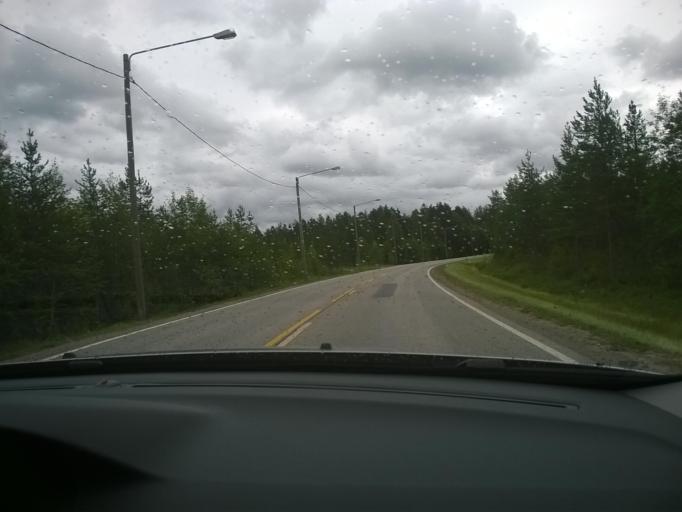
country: FI
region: Kainuu
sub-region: Kehys-Kainuu
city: Kuhmo
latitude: 64.1303
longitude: 29.4966
